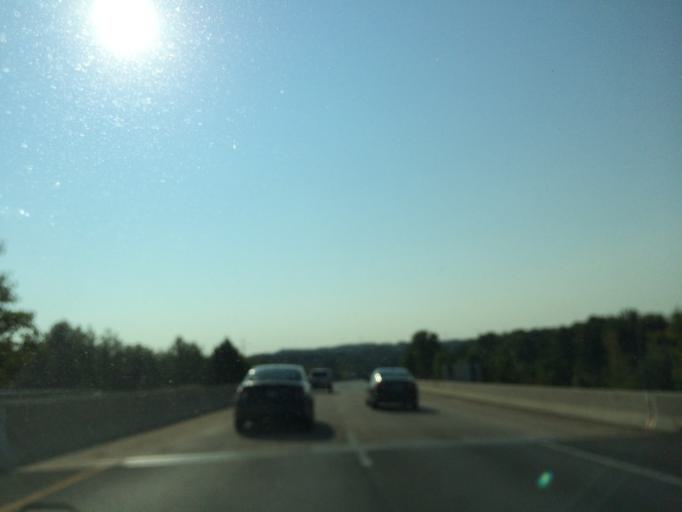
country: US
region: Maryland
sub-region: Anne Arundel County
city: Odenton
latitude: 39.1007
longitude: -76.6947
